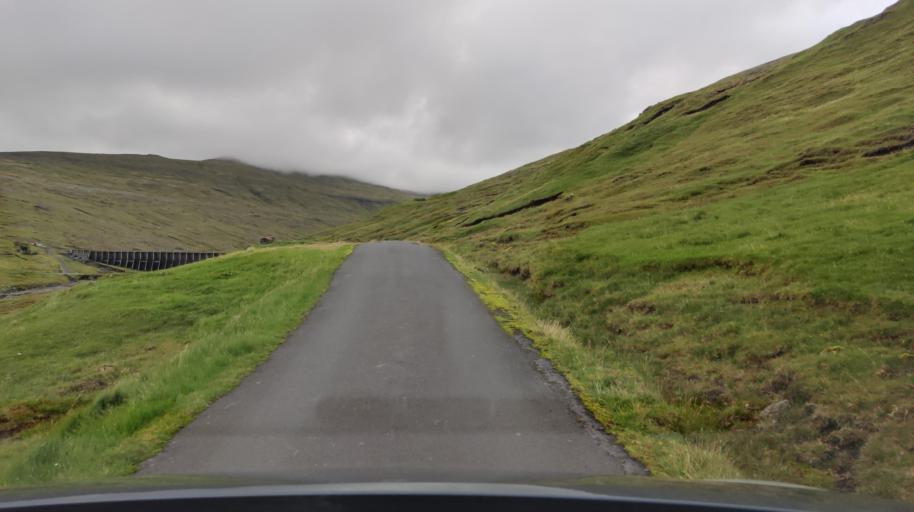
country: FO
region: Streymoy
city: Vestmanna
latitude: 62.1733
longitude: -7.1477
